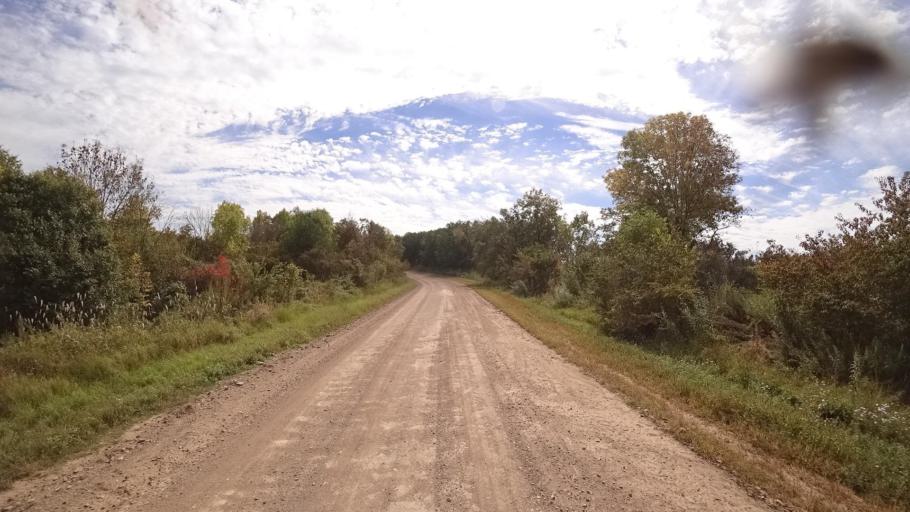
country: RU
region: Primorskiy
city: Yakovlevka
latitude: 44.5241
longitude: 133.5945
